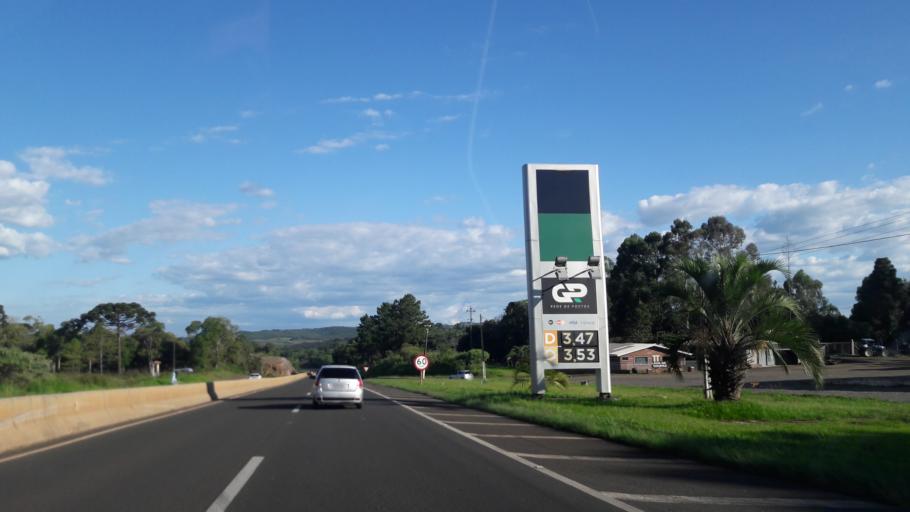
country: BR
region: Parana
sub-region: Guarapuava
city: Guarapuava
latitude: -25.3478
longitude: -51.3812
